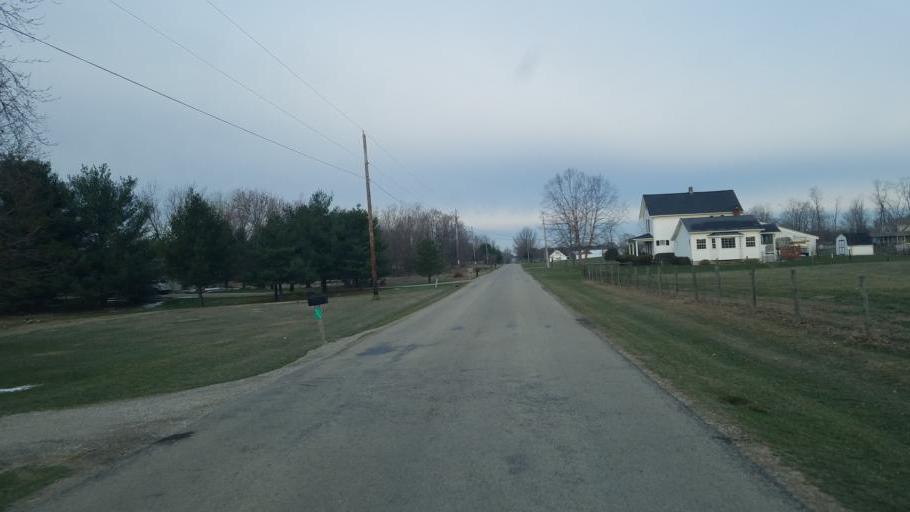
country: US
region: Ohio
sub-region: Morrow County
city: Cardington
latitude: 40.4104
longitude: -82.7917
